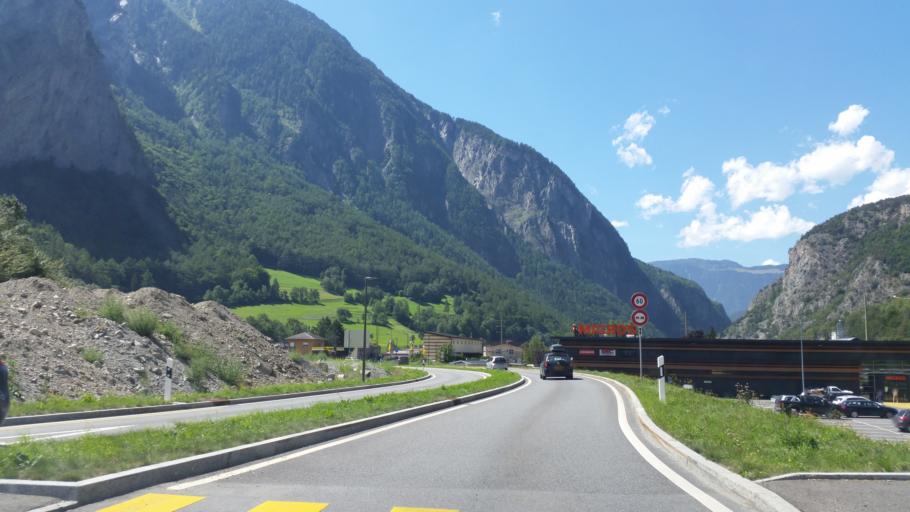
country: CH
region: Valais
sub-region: Martigny District
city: Charrat-les-Chenes
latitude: 46.0791
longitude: 7.1454
